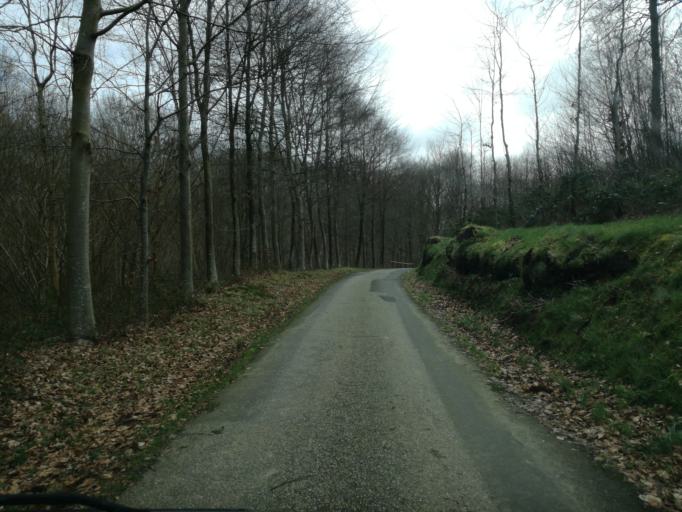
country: FR
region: Haute-Normandie
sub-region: Departement de la Seine-Maritime
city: Yebleron
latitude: 49.6828
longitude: 0.4925
